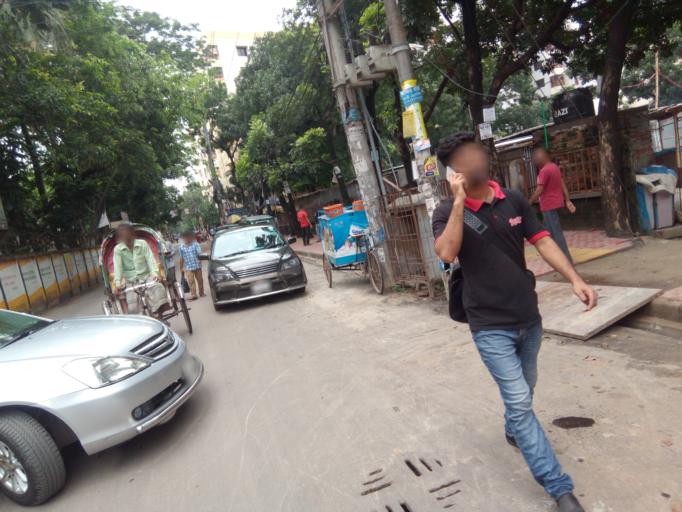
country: BD
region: Dhaka
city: Azimpur
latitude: 23.7581
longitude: 90.3722
